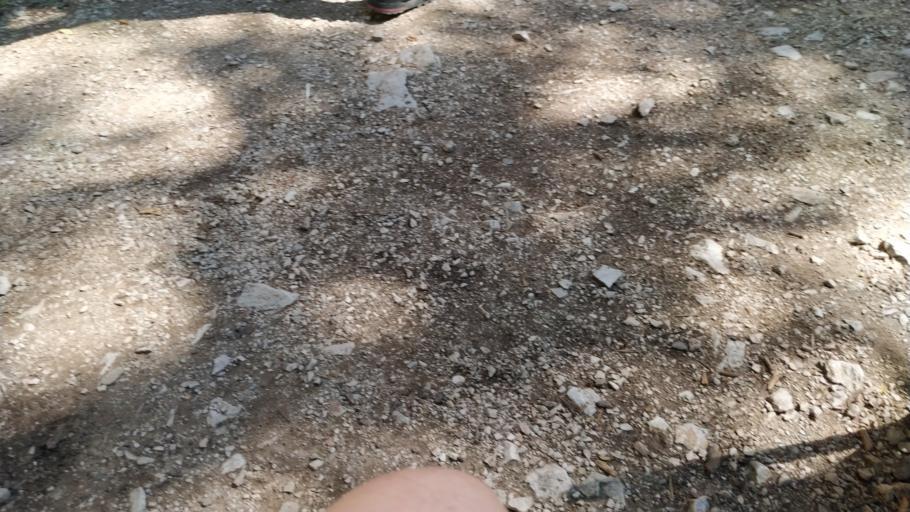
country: IT
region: Trentino-Alto Adige
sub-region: Provincia di Trento
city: Sanzeno
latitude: 46.3693
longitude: 11.0911
